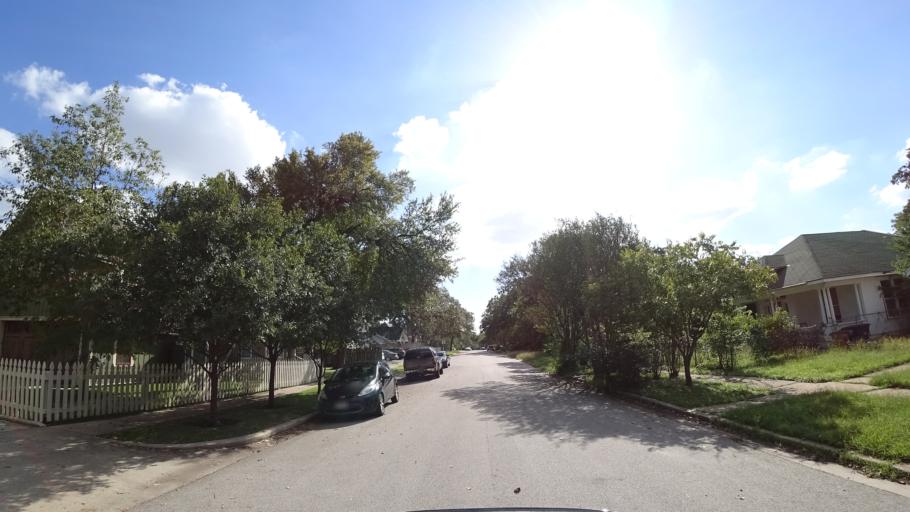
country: US
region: Texas
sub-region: Travis County
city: Austin
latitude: 30.3048
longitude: -97.7332
